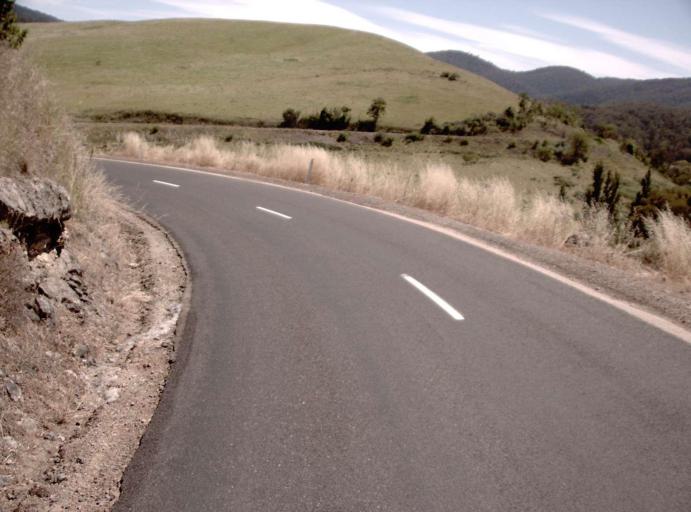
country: AU
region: Victoria
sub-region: East Gippsland
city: Lakes Entrance
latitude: -37.4156
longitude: 148.2064
